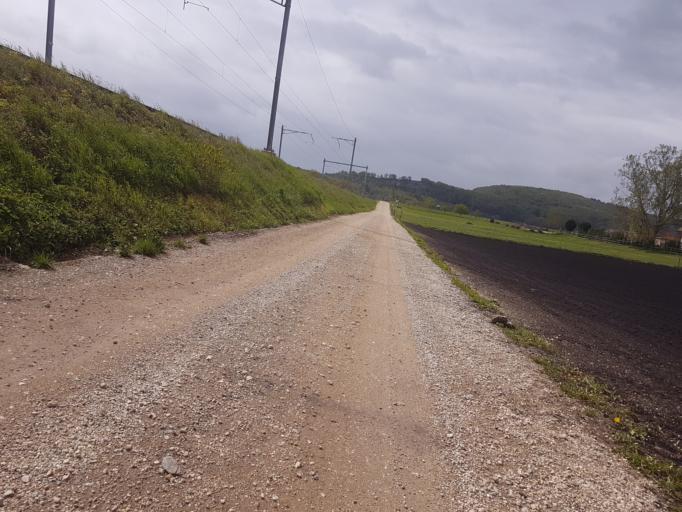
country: CH
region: Vaud
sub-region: Jura-Nord vaudois District
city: Bavois
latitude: 46.6746
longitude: 6.5542
